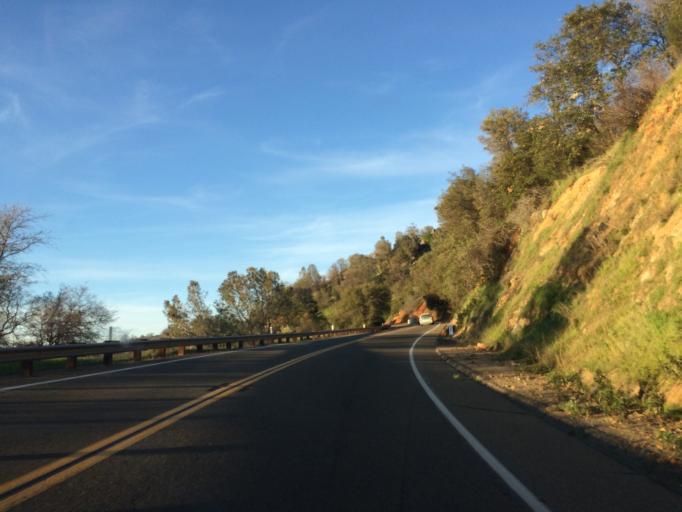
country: US
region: California
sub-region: Mariposa County
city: Mariposa
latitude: 37.4716
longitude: -120.0751
